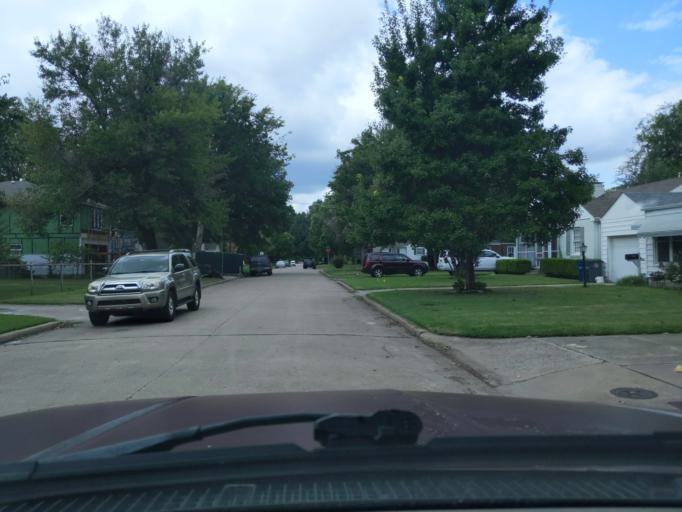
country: US
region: Oklahoma
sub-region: Tulsa County
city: Tulsa
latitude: 36.1107
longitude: -95.9771
